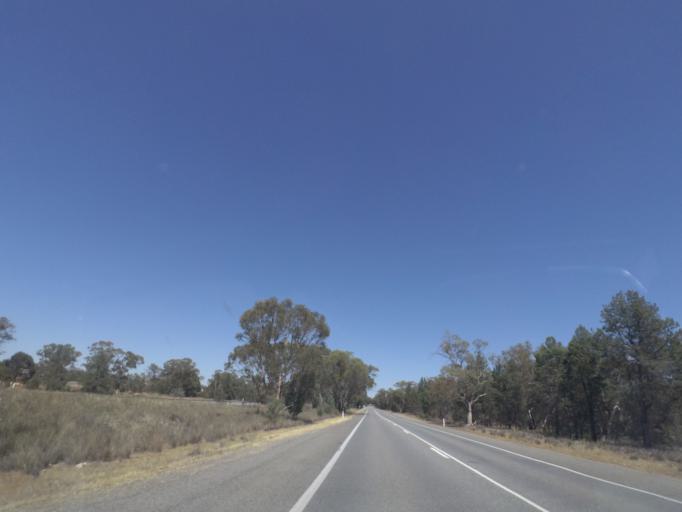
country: AU
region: New South Wales
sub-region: Narrandera
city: Narrandera
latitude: -34.7381
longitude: 146.5802
